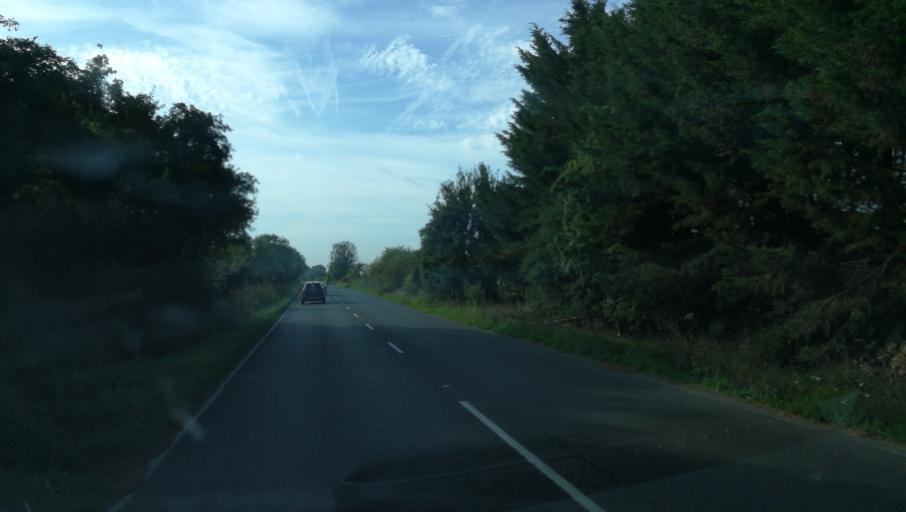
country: GB
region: England
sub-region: Oxfordshire
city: Woodstock
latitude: 51.8681
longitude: -1.3275
